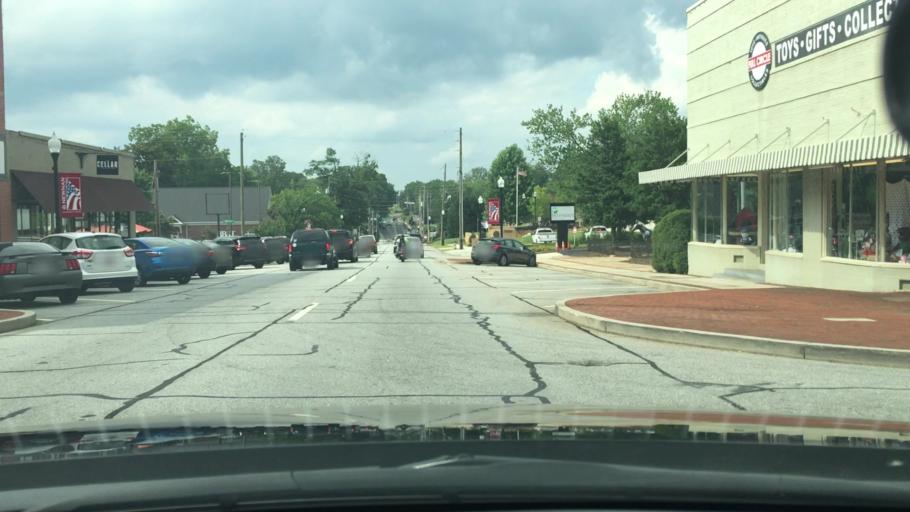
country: US
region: Georgia
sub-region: Coweta County
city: Newnan
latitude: 33.3759
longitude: -84.7994
